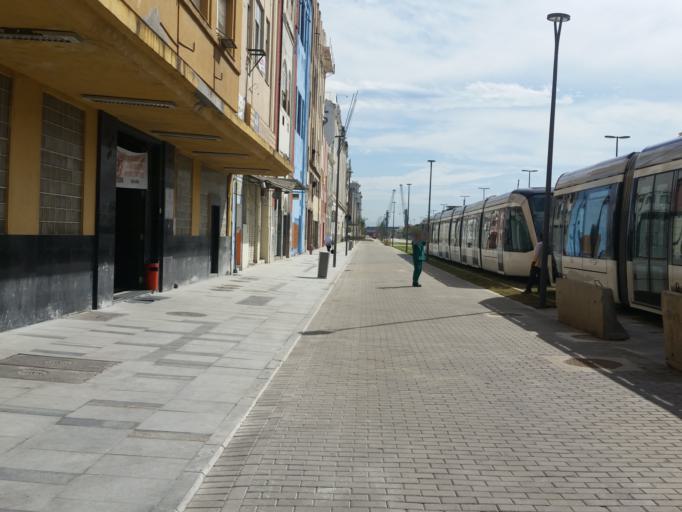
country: BR
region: Rio de Janeiro
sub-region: Rio De Janeiro
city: Rio de Janeiro
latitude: -22.8952
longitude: -43.1844
